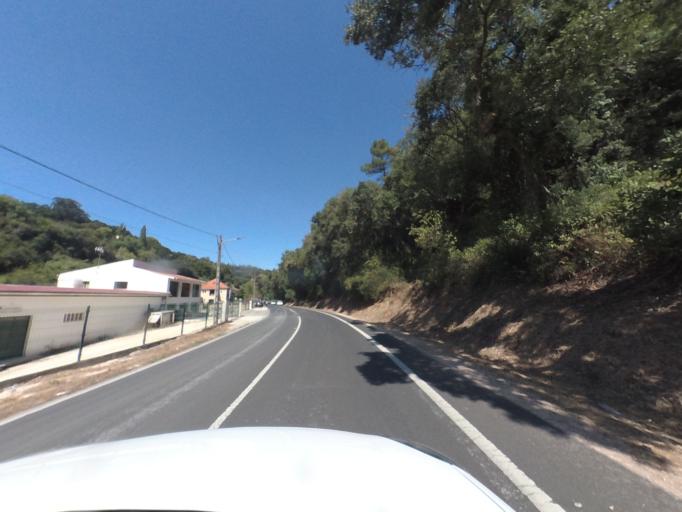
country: PT
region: Leiria
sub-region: Alcobaca
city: Alcobaca
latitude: 39.5423
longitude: -8.9863
